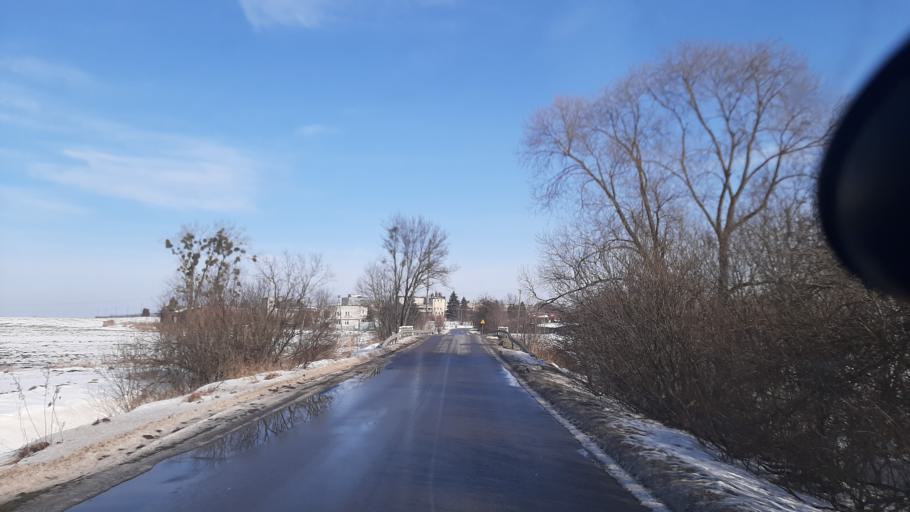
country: PL
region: Lublin Voivodeship
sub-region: Powiat pulawski
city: Kurow
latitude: 51.3835
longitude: 22.1654
